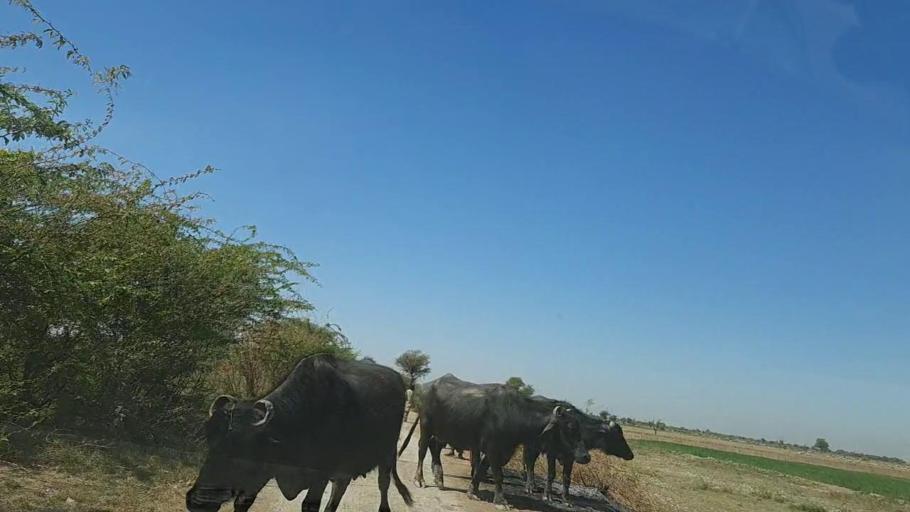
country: PK
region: Sindh
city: Dhoro Naro
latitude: 25.4888
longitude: 69.5238
